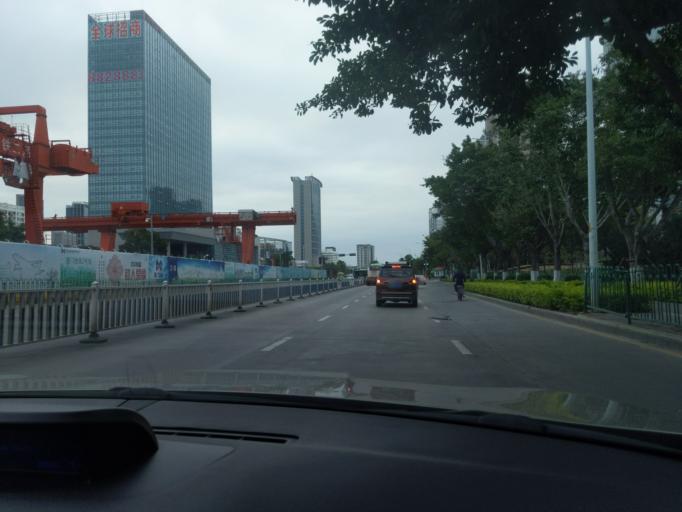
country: CN
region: Fujian
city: Liuwudian
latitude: 24.4853
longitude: 118.1738
